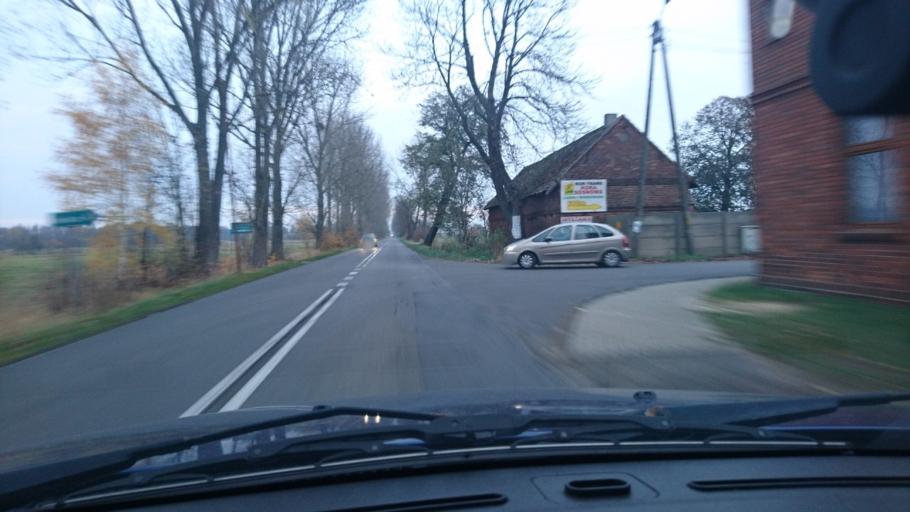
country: PL
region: Greater Poland Voivodeship
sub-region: Powiat ostrowski
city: Odolanow
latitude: 51.5453
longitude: 17.6559
